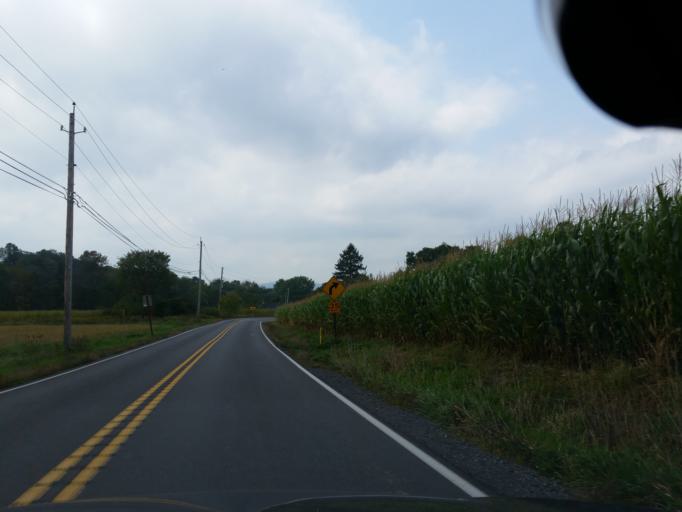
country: US
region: Pennsylvania
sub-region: Union County
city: Mifflinburg
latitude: 40.9844
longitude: -77.0053
